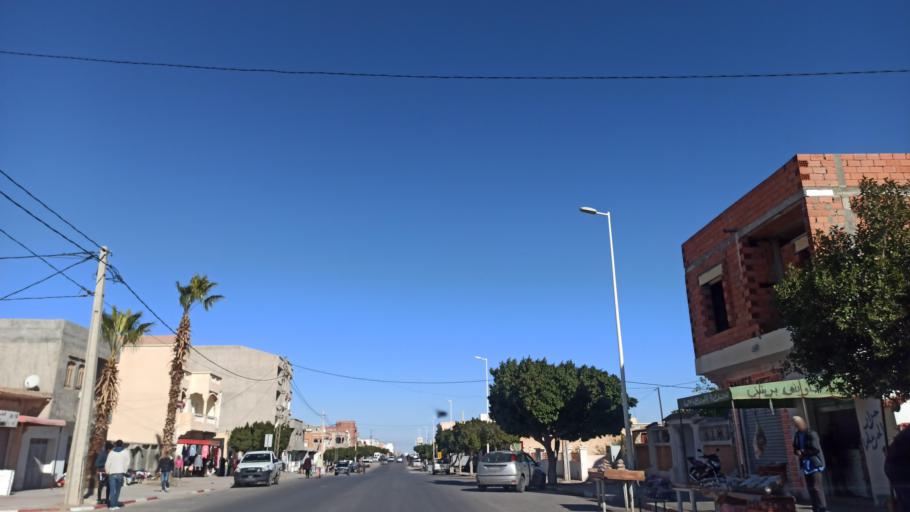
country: TN
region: Sidi Bu Zayd
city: Bi'r al Hufayy
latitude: 34.9368
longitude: 9.1998
